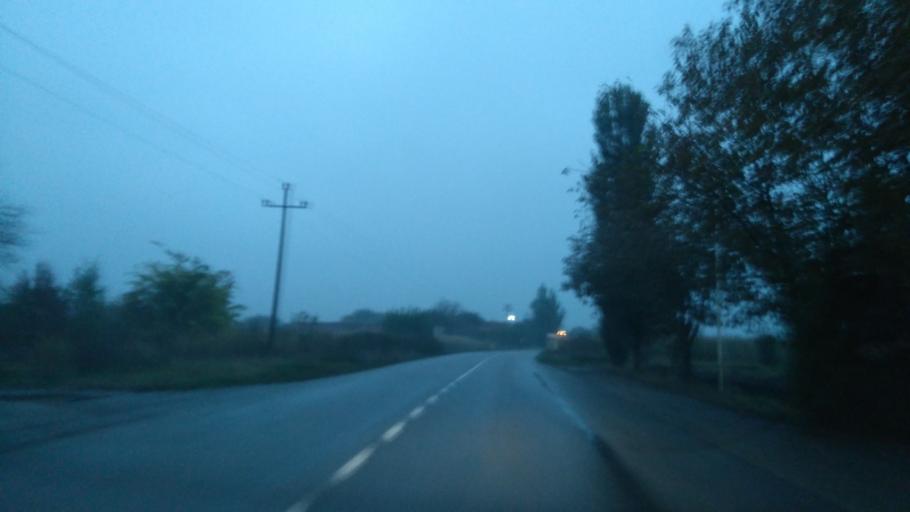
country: RS
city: Mol
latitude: 45.7516
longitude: 20.1277
